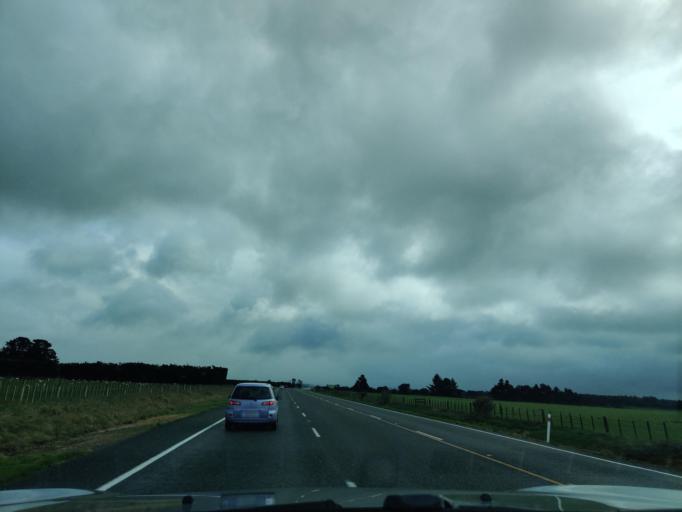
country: NZ
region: Hawke's Bay
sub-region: Hastings District
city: Hastings
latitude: -40.0208
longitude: 176.3080
